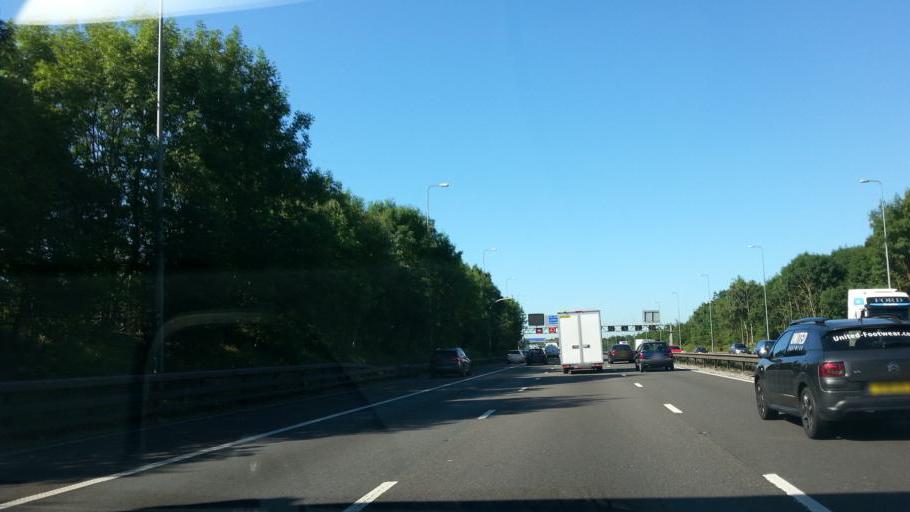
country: GB
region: England
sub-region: Solihull
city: Solihull
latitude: 52.3879
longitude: -1.7779
